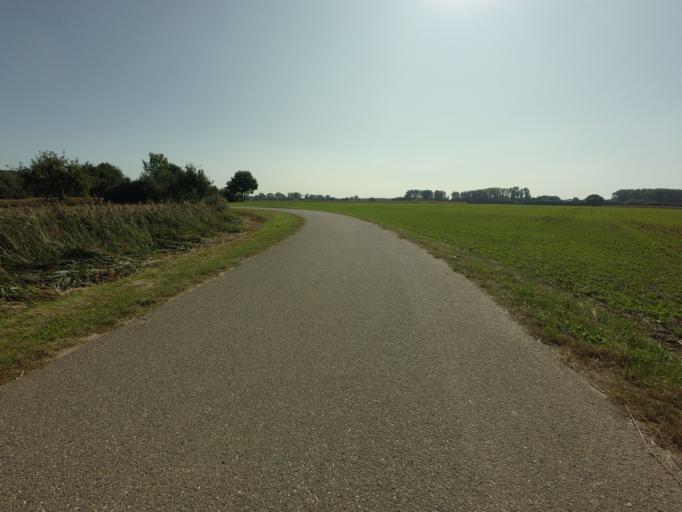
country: NL
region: Limburg
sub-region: Gemeente Roerdalen
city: Melick
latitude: 51.1542
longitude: 6.0317
